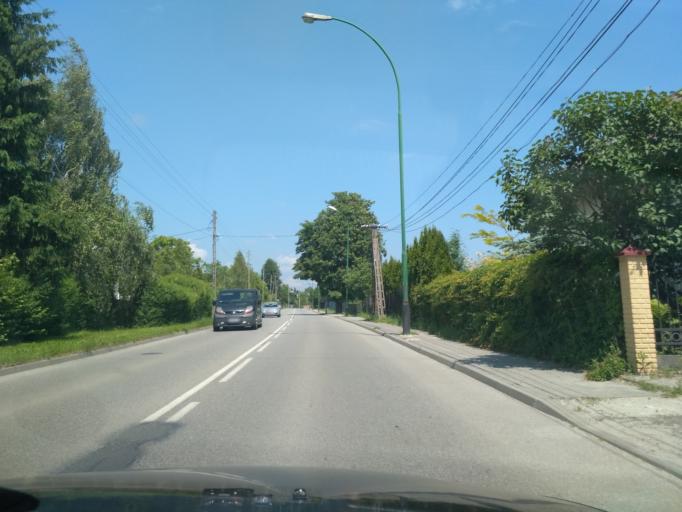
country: PL
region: Subcarpathian Voivodeship
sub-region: Powiat lancucki
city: Lancut
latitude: 50.0539
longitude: 22.2244
